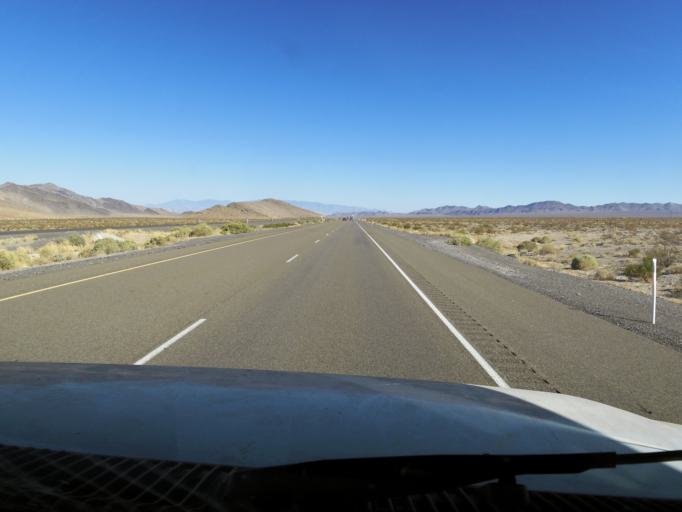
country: US
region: Nevada
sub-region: Nye County
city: Pahrump
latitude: 36.5715
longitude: -115.8676
